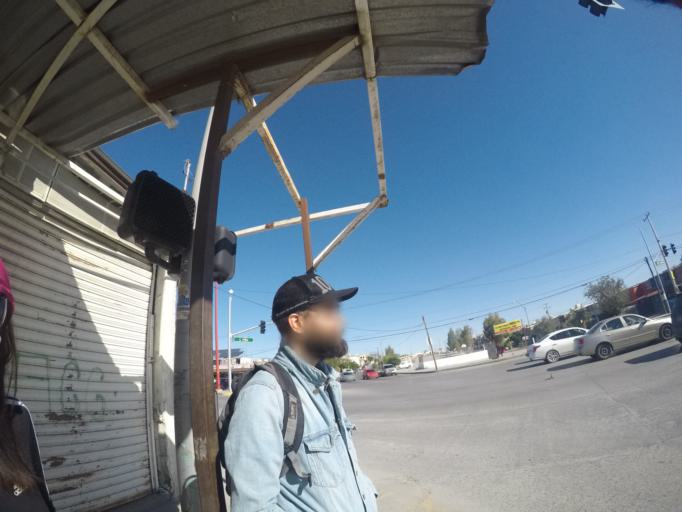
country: US
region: Texas
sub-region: El Paso County
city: Socorro
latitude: 31.6656
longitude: -106.4014
